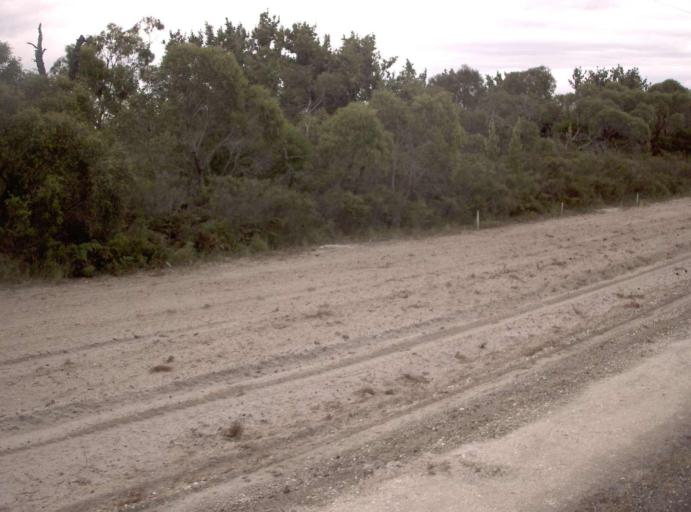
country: AU
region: Victoria
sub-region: East Gippsland
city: Bairnsdale
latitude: -38.0866
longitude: 147.5243
